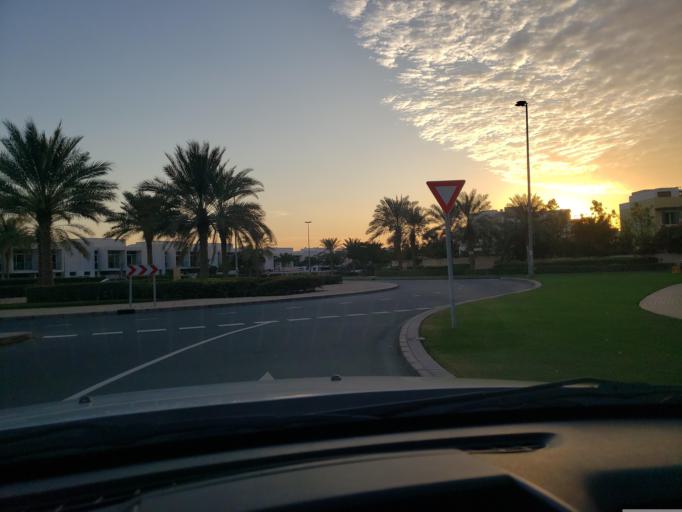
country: AE
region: Dubai
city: Dubai
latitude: 25.0207
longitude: 55.2740
